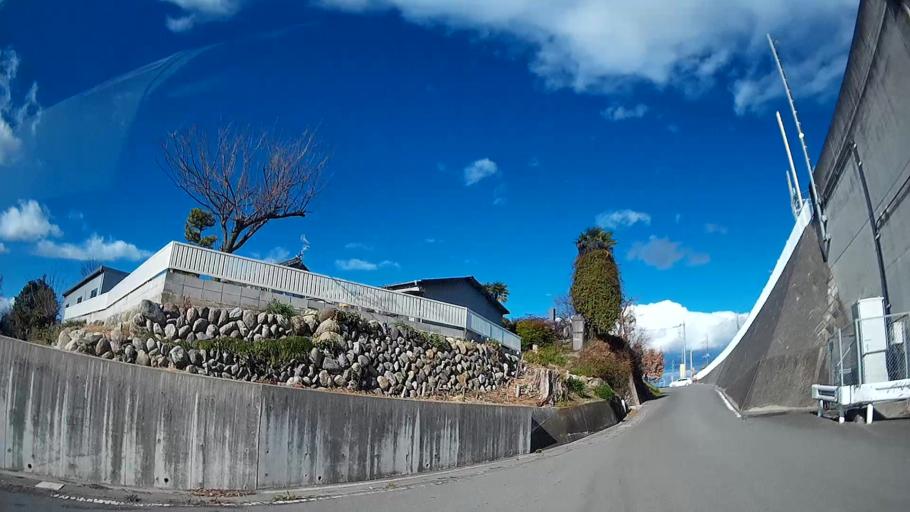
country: JP
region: Saitama
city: Yorii
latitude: 36.1192
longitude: 139.2419
